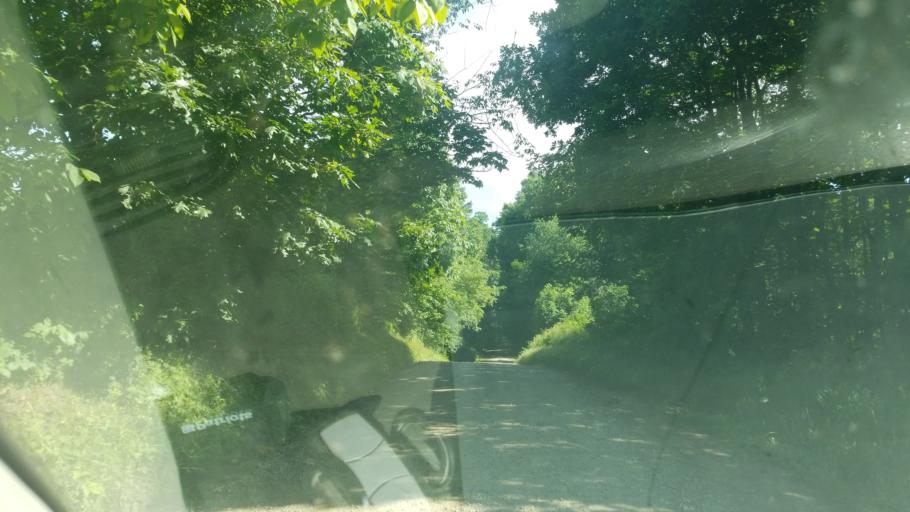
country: US
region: Ohio
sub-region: Holmes County
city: Millersburg
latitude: 40.4525
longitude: -81.9476
